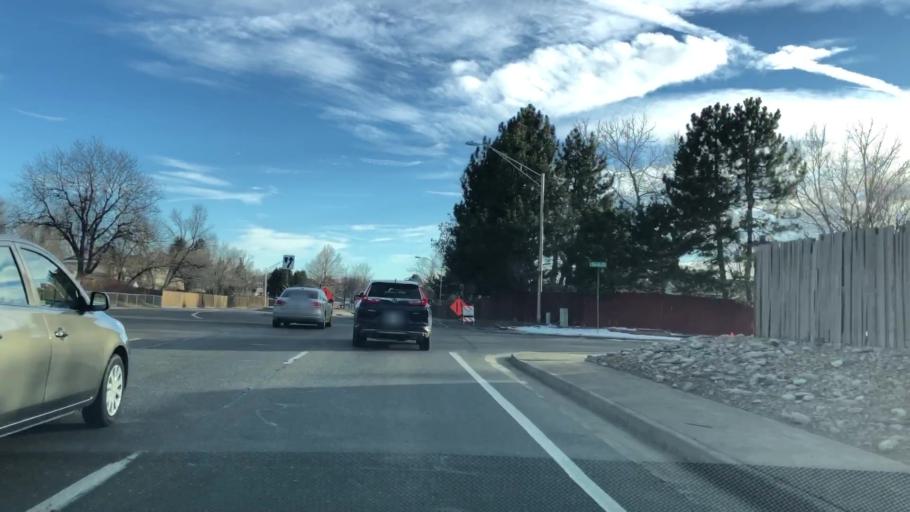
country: US
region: Colorado
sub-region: Adams County
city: Aurora
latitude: 39.6568
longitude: -104.7915
